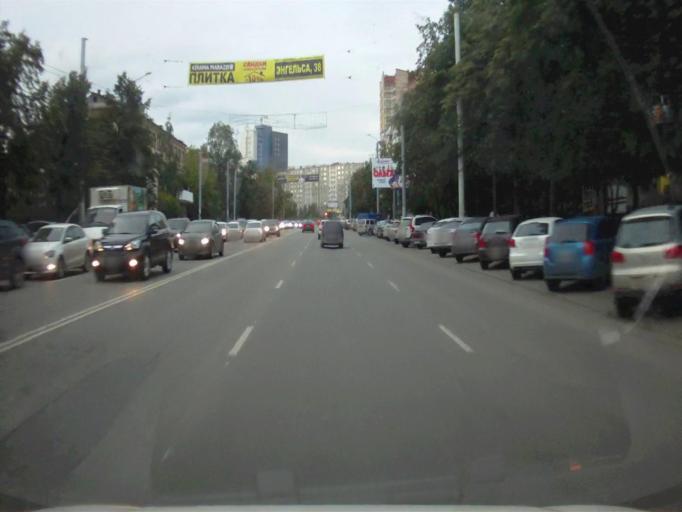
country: RU
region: Chelyabinsk
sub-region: Gorod Chelyabinsk
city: Chelyabinsk
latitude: 55.1565
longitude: 61.3815
